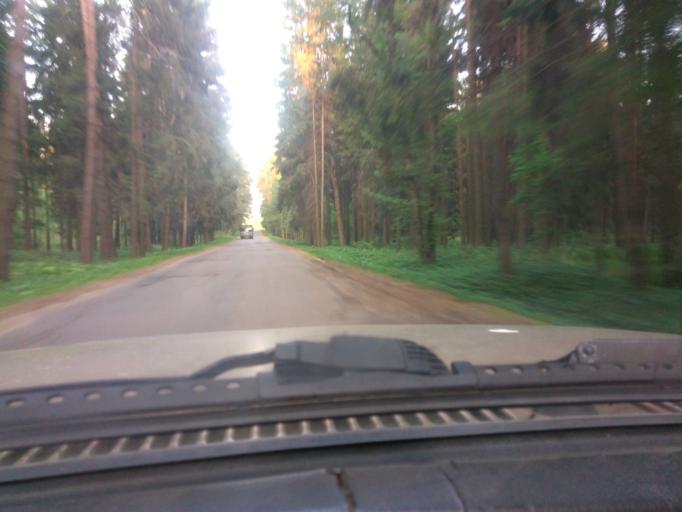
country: BY
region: Mogilev
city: Mahilyow
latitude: 53.9311
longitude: 30.3013
